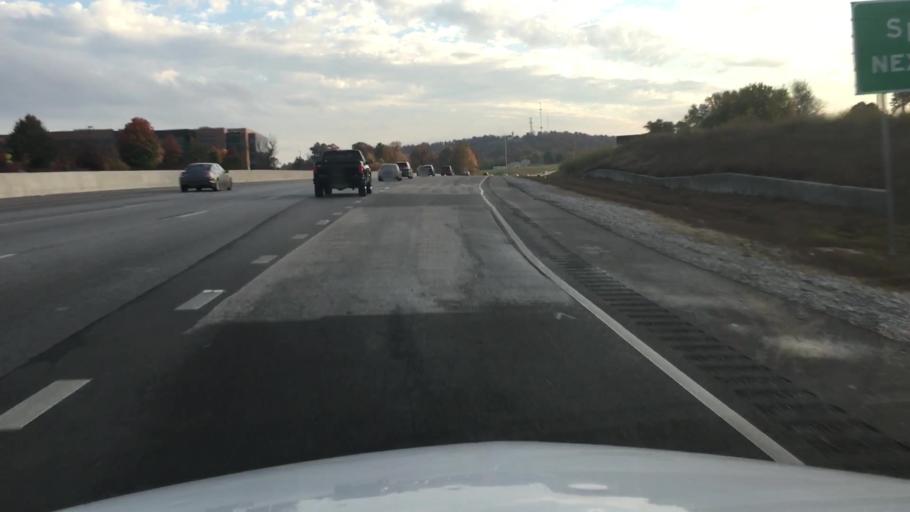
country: US
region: Arkansas
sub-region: Benton County
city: Lowell
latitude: 36.2481
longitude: -94.1508
